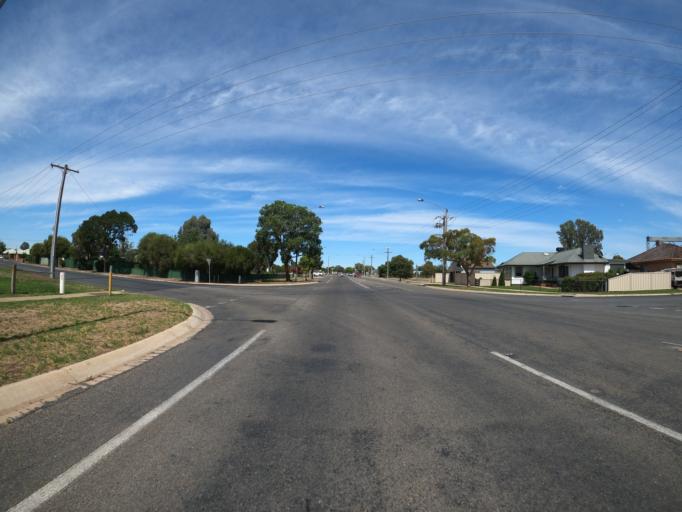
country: AU
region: Victoria
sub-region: Moira
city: Yarrawonga
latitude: -36.0189
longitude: 146.0007
